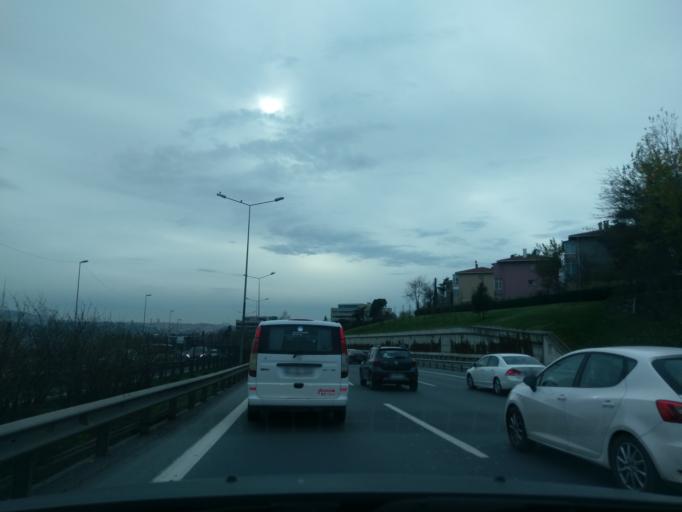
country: TR
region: Istanbul
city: Sisli
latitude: 41.0613
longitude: 29.0161
